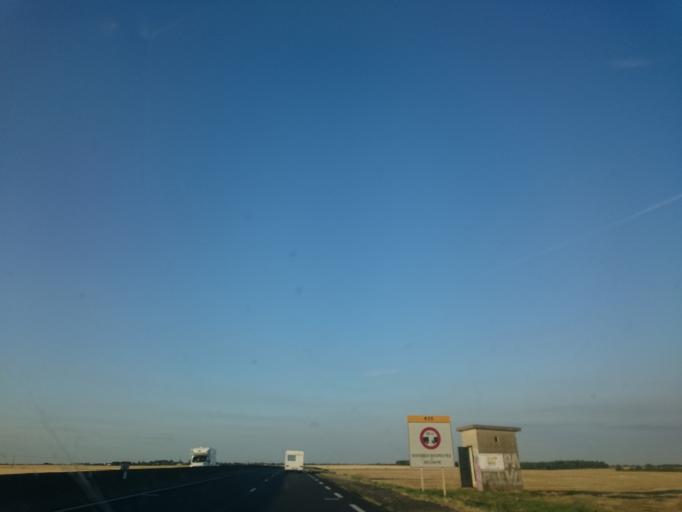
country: FR
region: Ile-de-France
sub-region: Departement de l'Essonne
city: Angerville
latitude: 48.3289
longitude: 2.0238
